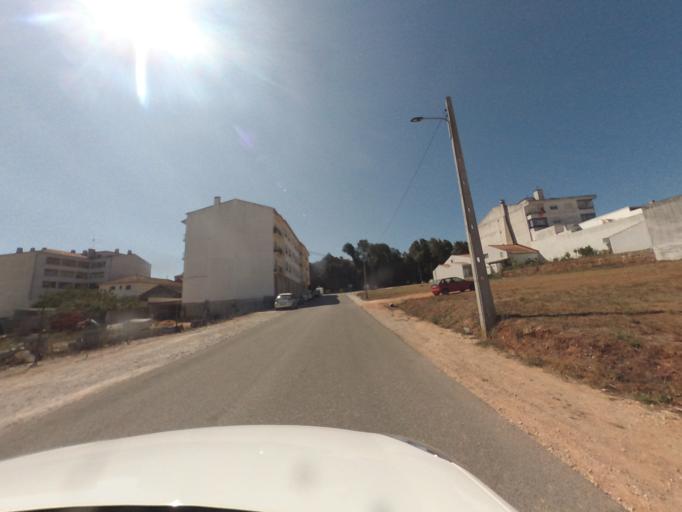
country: PT
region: Leiria
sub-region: Alcobaca
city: Turquel
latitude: 39.4657
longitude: -8.9773
